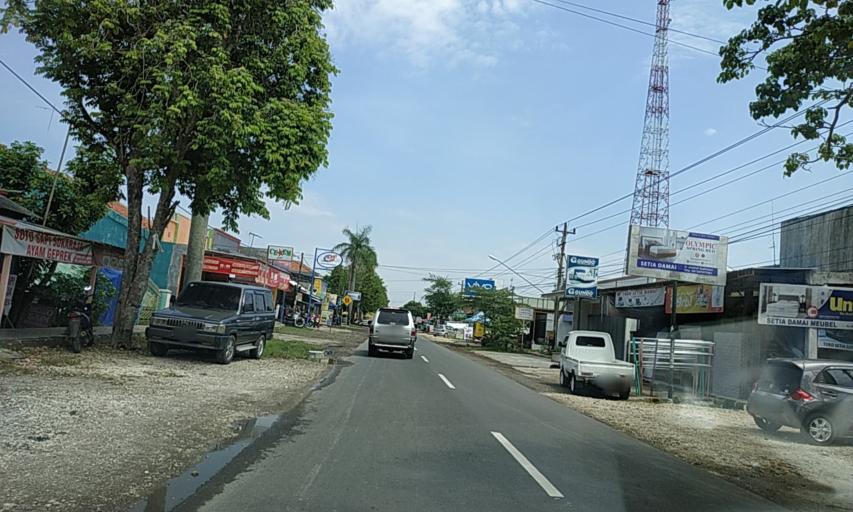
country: ID
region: Central Java
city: Sidareja
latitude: -7.4855
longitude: 108.7967
